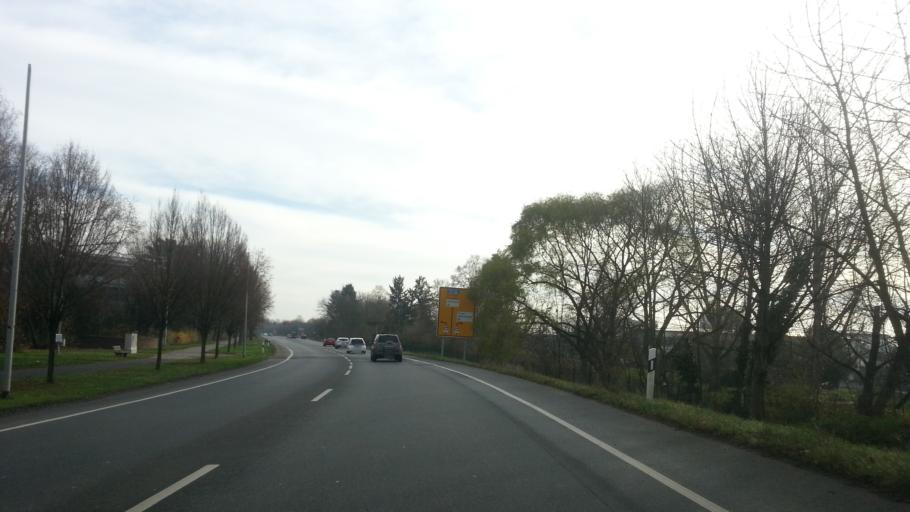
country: DE
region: Hesse
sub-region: Regierungsbezirk Darmstadt
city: Gross-Gerau
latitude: 49.9172
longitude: 8.4761
